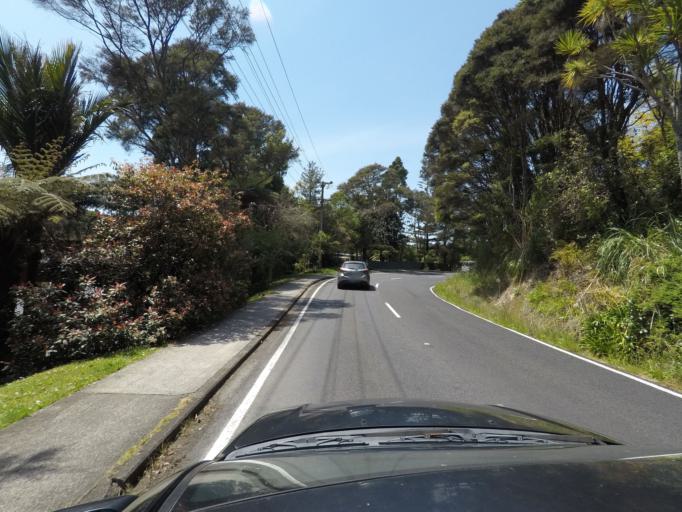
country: NZ
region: Auckland
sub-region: Auckland
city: Titirangi
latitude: -36.9576
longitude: 174.6380
